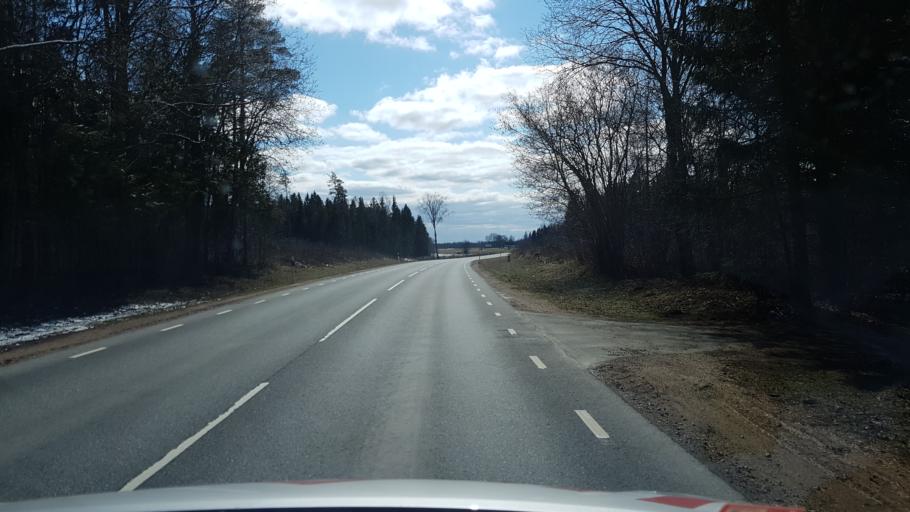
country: EE
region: Laeaene-Virumaa
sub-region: Kadrina vald
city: Kadrina
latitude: 59.3878
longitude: 26.0167
